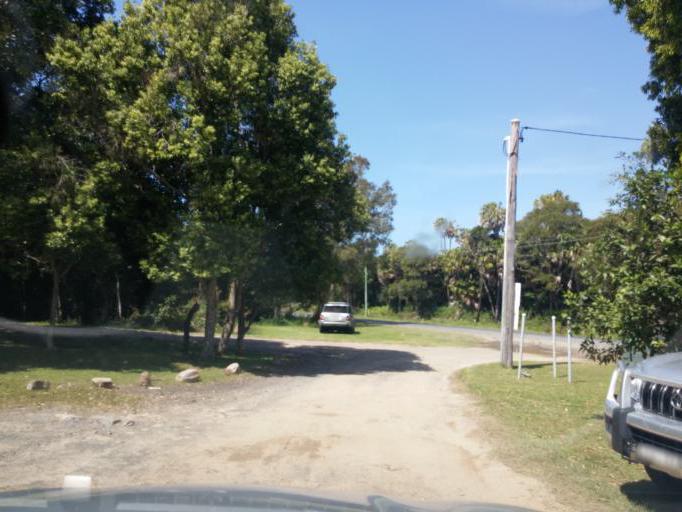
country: AU
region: New South Wales
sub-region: Great Lakes
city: Forster
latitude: -32.3311
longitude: 152.5369
